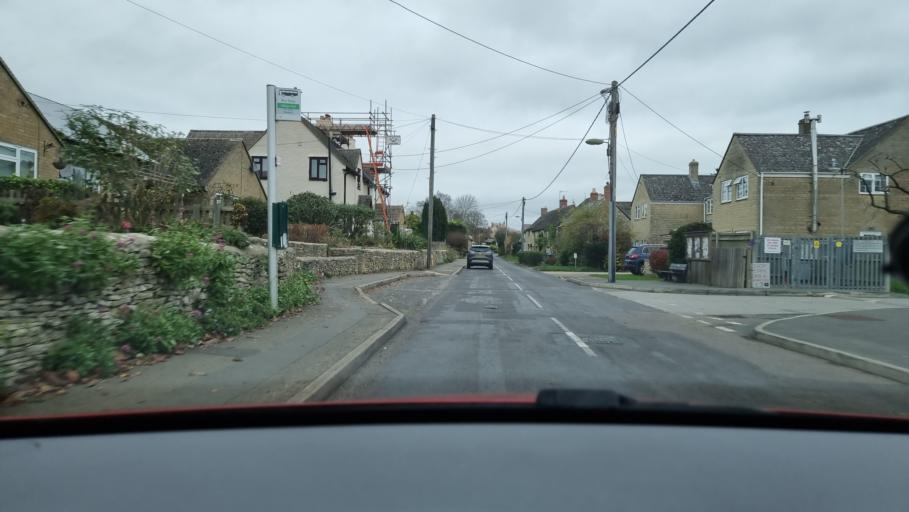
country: GB
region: England
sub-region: Oxfordshire
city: Woodstock
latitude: 51.8830
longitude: -1.3051
